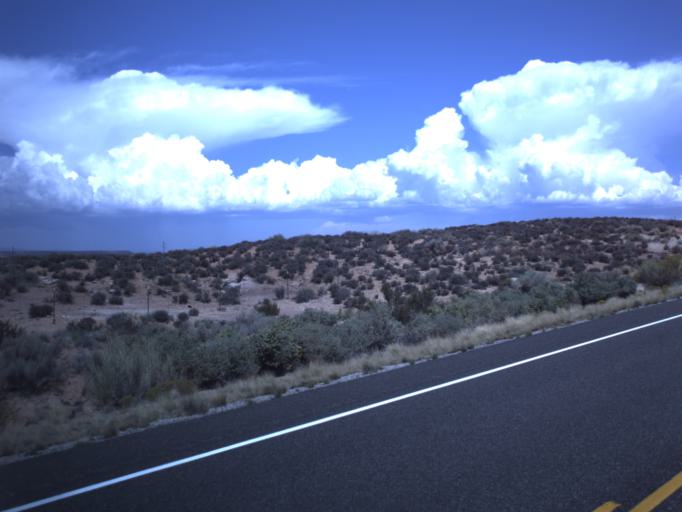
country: US
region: Utah
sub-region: San Juan County
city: Blanding
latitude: 37.3665
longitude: -109.5088
